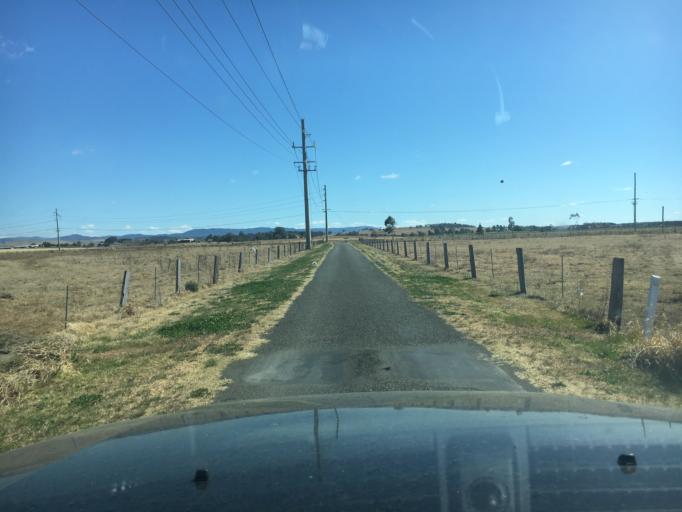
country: AU
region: New South Wales
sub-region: Singleton
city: Singleton
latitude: -32.5900
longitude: 151.1683
